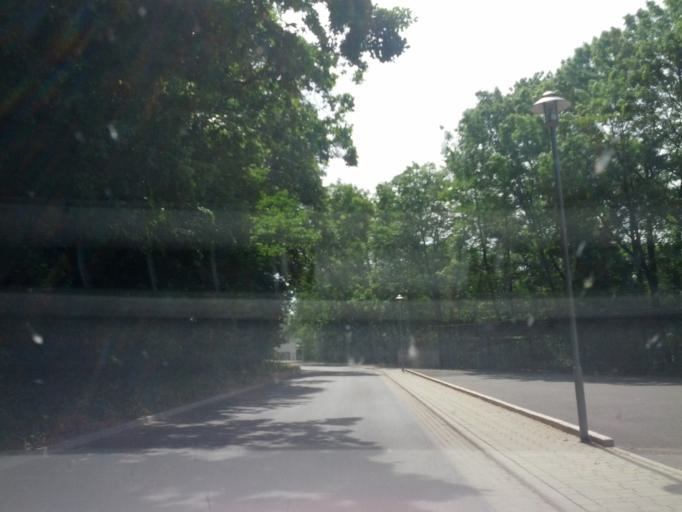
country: DE
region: Thuringia
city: Thal
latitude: 50.9572
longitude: 10.4021
